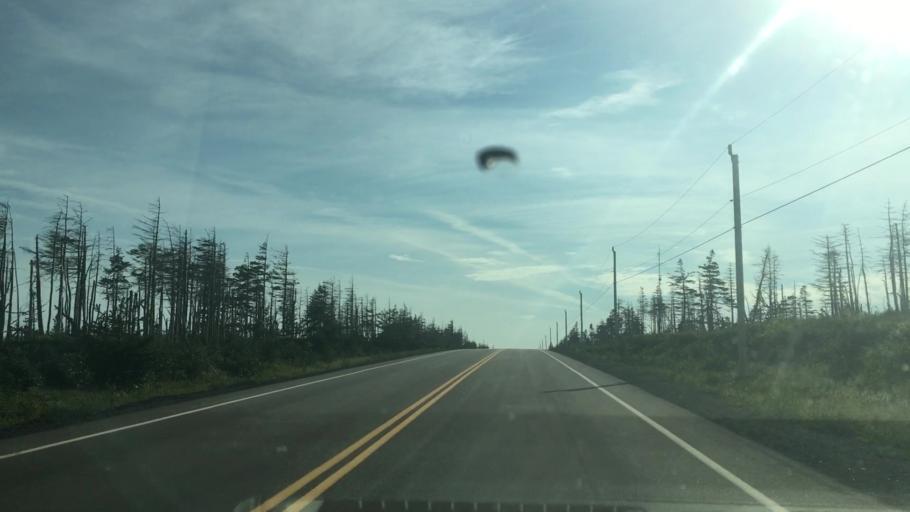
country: CA
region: Nova Scotia
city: Sydney Mines
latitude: 46.8213
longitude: -60.6649
